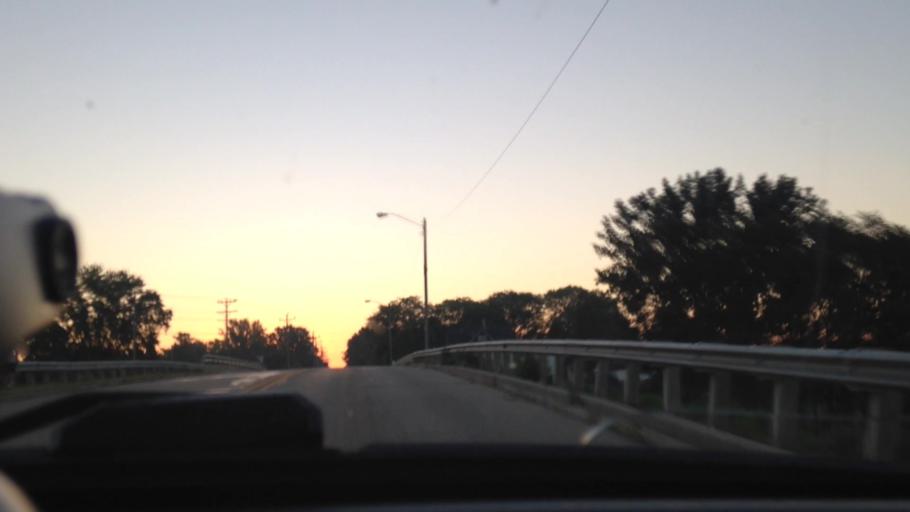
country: US
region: Wisconsin
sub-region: Dodge County
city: Lomira
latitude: 43.5871
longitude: -88.4423
